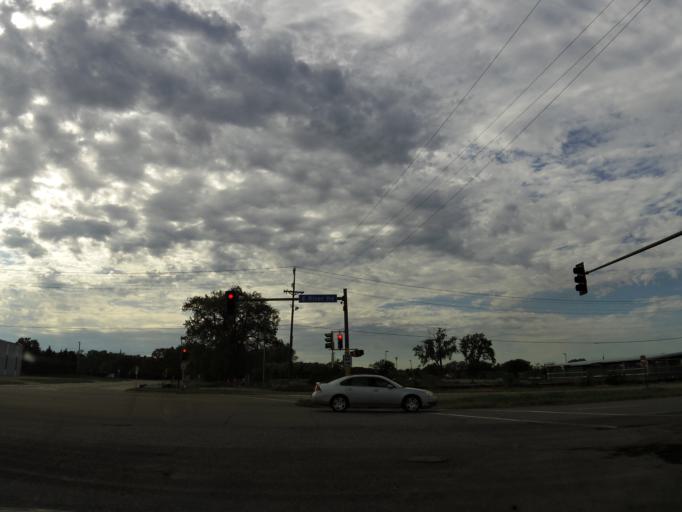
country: US
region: Minnesota
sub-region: Anoka County
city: Columbia Heights
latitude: 45.0355
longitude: -93.2755
